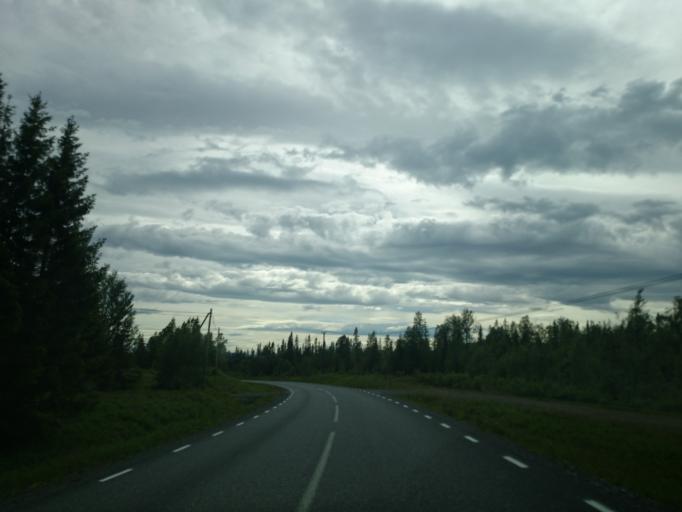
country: SE
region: Jaemtland
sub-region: Are Kommun
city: Are
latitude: 63.2441
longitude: 13.1815
